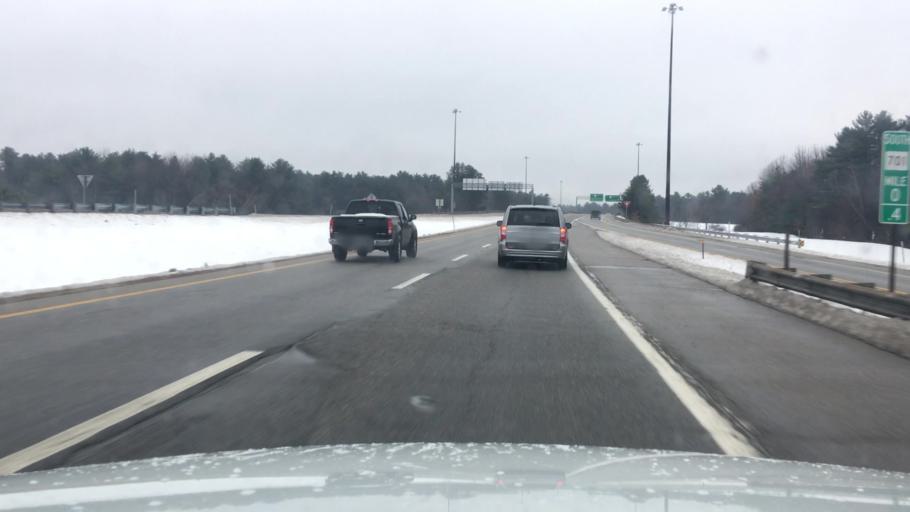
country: US
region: Maine
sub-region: Cumberland County
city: South Portland Gardens
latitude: 43.6264
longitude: -70.3189
